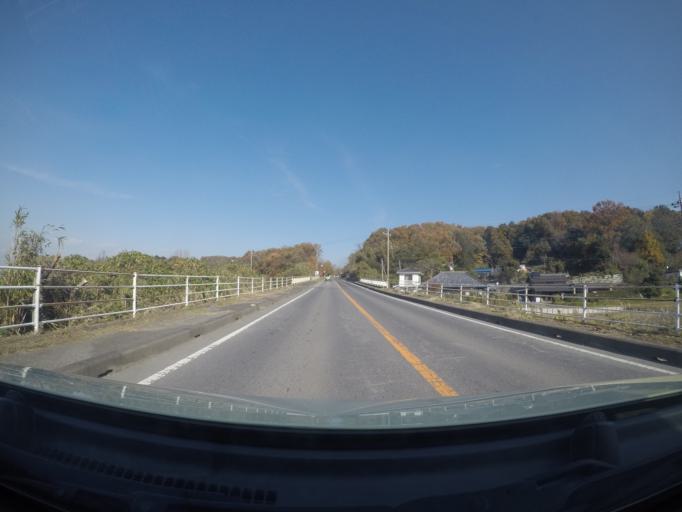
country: JP
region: Ibaraki
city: Makabe
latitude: 36.2628
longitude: 140.0913
